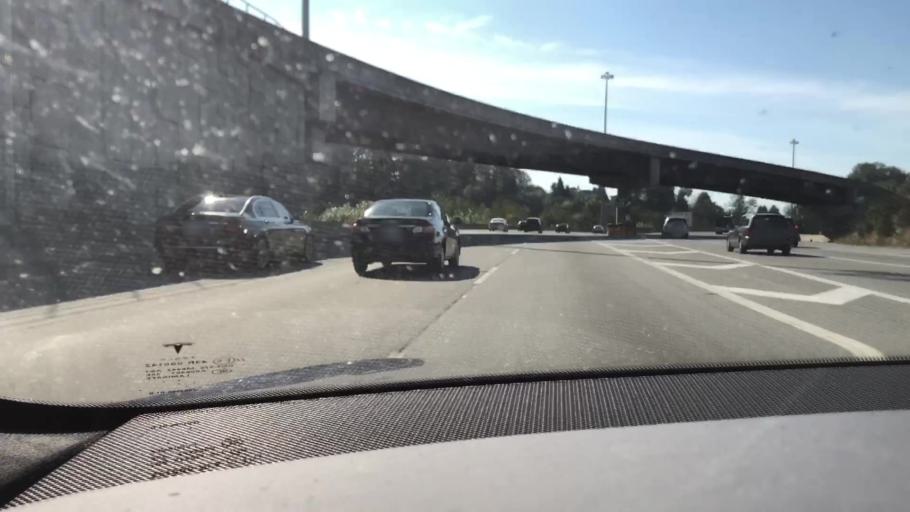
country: CA
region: British Columbia
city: Burnaby
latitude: 49.2581
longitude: -123.0155
